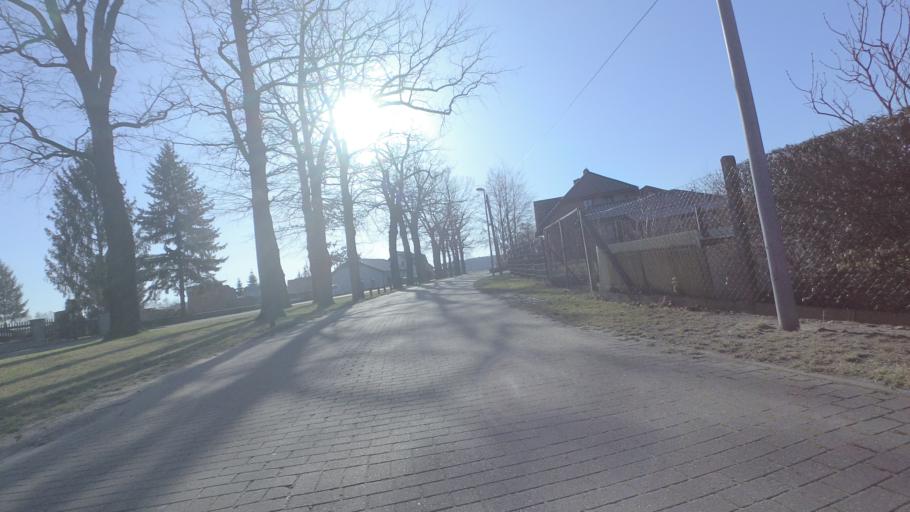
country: DE
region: Brandenburg
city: Luckenwalde
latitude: 52.0594
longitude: 13.1668
